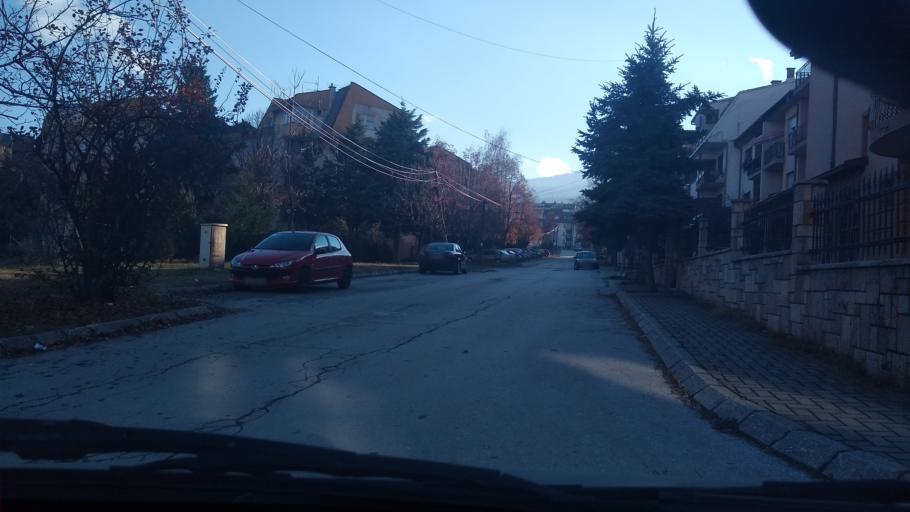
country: MK
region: Bitola
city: Bitola
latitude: 41.0247
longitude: 21.3151
